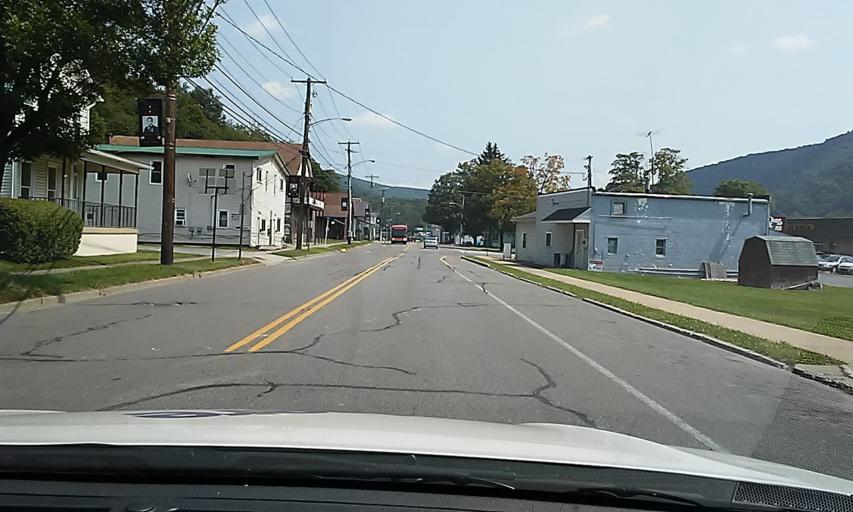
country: US
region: Pennsylvania
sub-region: Cameron County
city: Emporium
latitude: 41.5107
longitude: -78.2275
